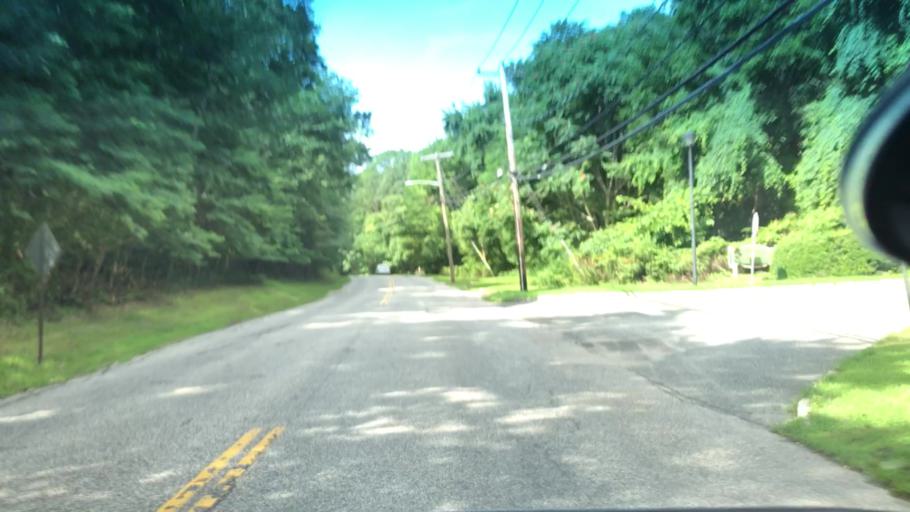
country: US
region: New York
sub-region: Suffolk County
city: Wading River
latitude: 40.9586
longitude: -72.8397
